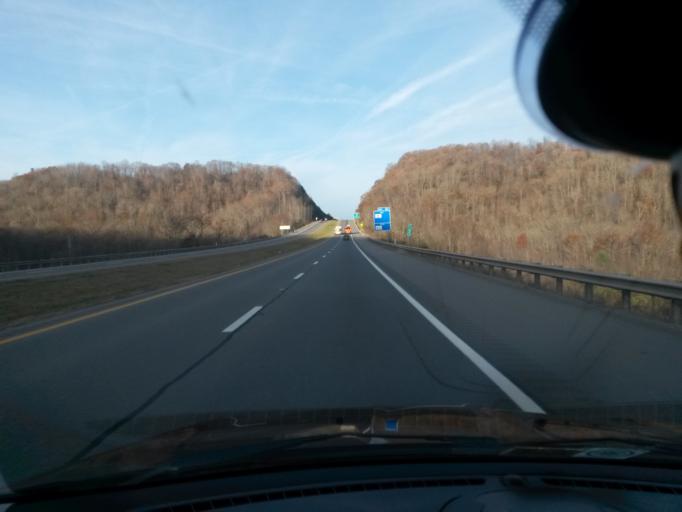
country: US
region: West Virginia
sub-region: Greenbrier County
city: Lewisburg
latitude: 37.8626
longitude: -80.5359
